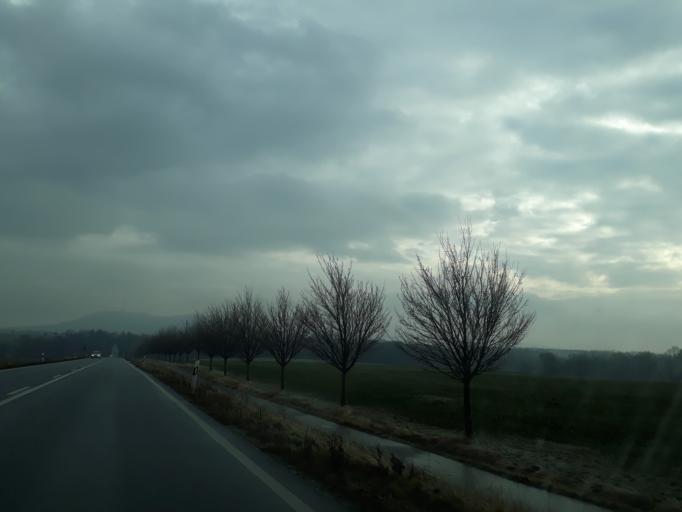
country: DE
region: Saxony
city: Lobau
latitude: 51.1234
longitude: 14.6310
